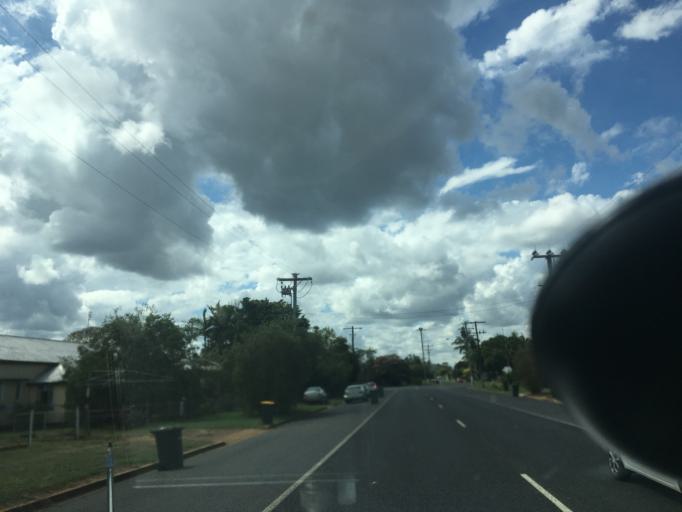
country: AU
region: Queensland
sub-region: Tablelands
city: Mareeba
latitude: -17.0025
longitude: 145.4252
